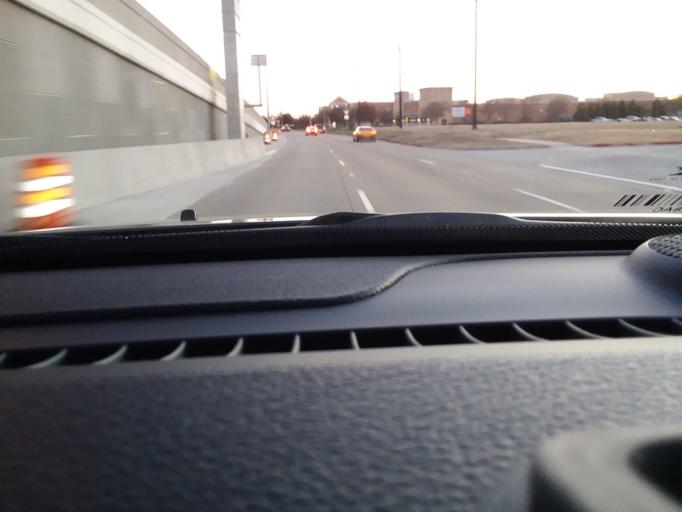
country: US
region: Texas
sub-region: Denton County
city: The Colony
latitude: 33.0579
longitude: -96.8297
